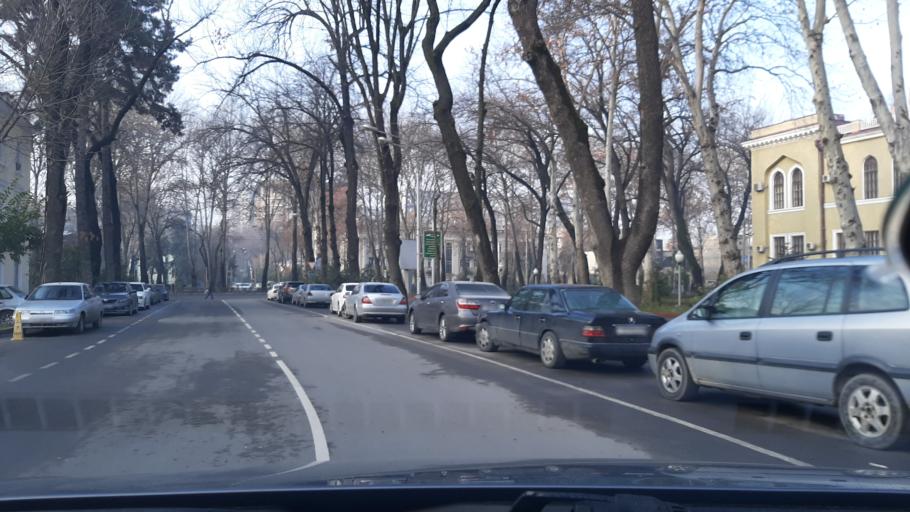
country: TJ
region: Dushanbe
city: Dushanbe
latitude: 38.5704
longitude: 68.7919
